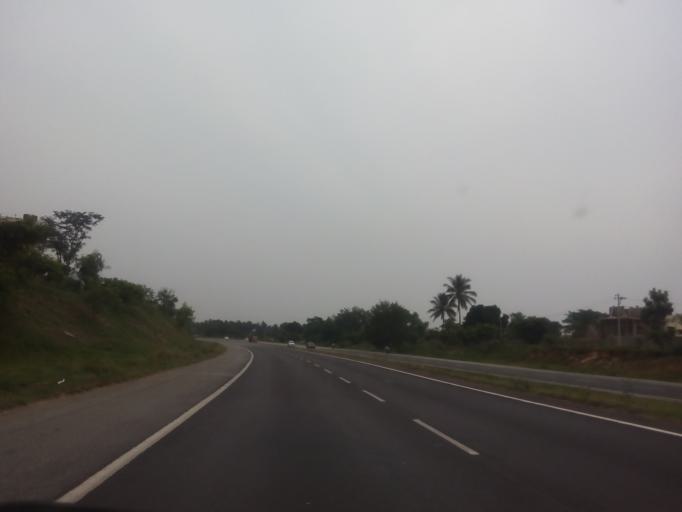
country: IN
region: Karnataka
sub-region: Bangalore Urban
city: Bangalore
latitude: 12.9852
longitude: 77.4712
